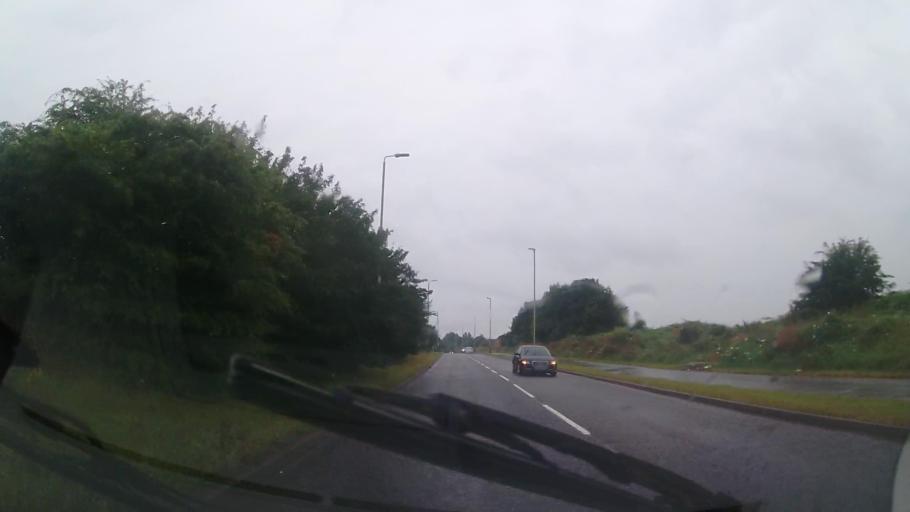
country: GB
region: England
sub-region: Leicestershire
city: Mountsorrel
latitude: 52.6778
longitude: -1.1478
